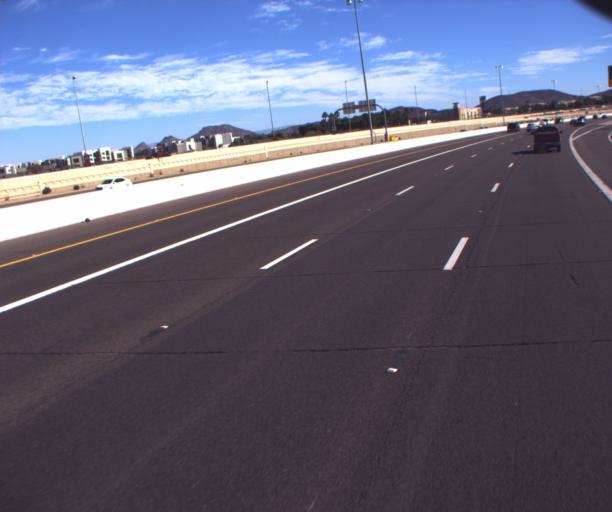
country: US
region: Arizona
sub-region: Maricopa County
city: Sun City
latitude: 33.6662
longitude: -112.2266
